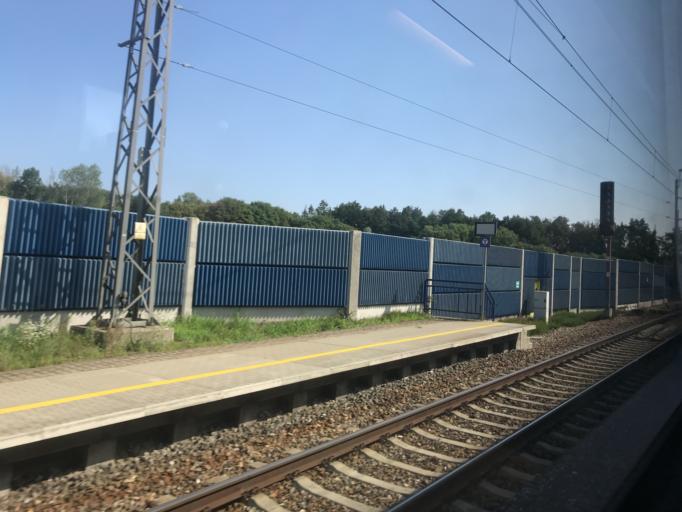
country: CZ
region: Central Bohemia
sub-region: Okres Benesov
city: Cercany
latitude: 49.8618
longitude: 14.7000
